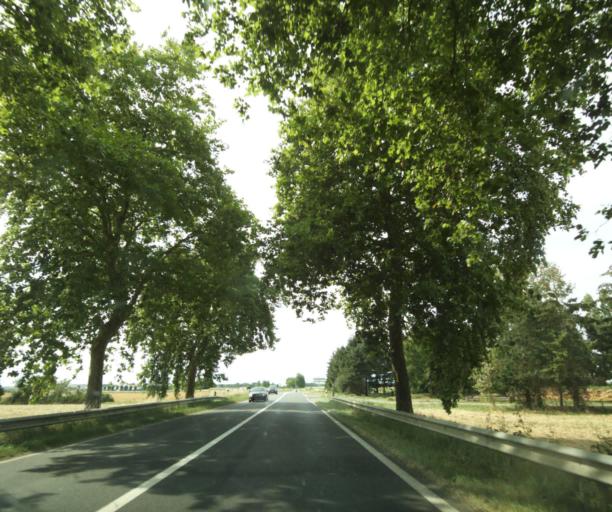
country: FR
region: Centre
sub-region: Departement d'Indre-et-Loire
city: Saint-Paterne-Racan
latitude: 47.5949
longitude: 0.5293
